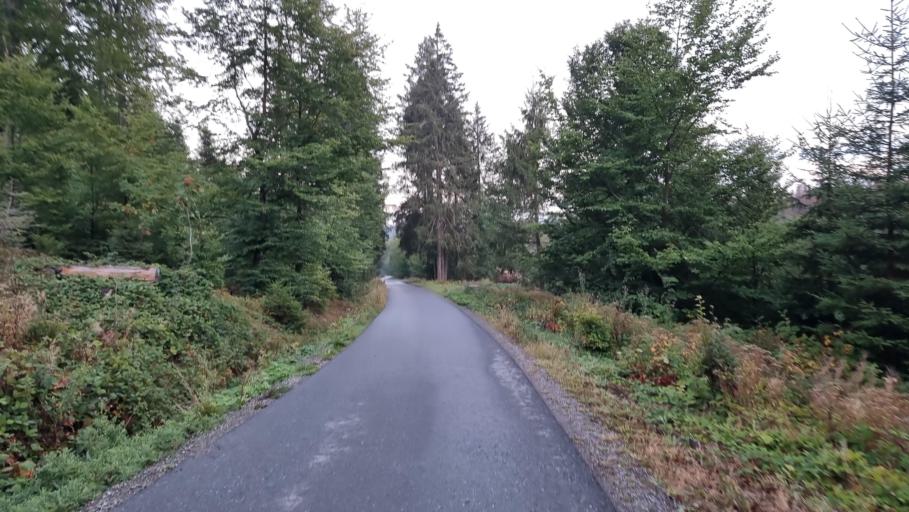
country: DE
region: Lower Saxony
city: Braunlage
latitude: 51.7426
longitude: 10.6085
